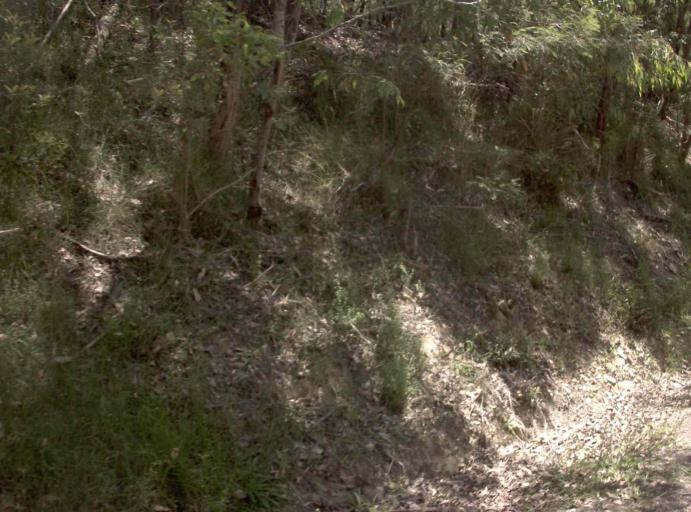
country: AU
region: New South Wales
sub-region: Bombala
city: Bombala
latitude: -37.5150
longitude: 148.9285
